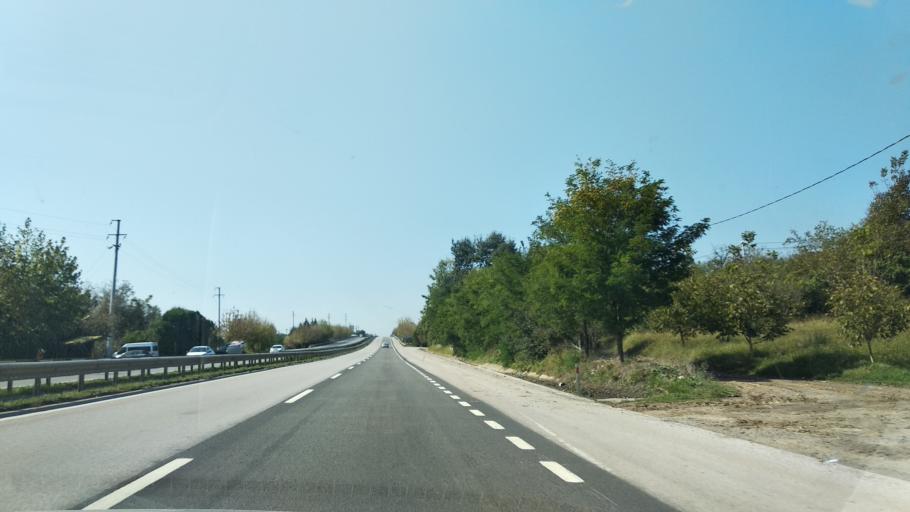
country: TR
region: Kocaeli
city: Derbent
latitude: 40.7321
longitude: 30.1839
